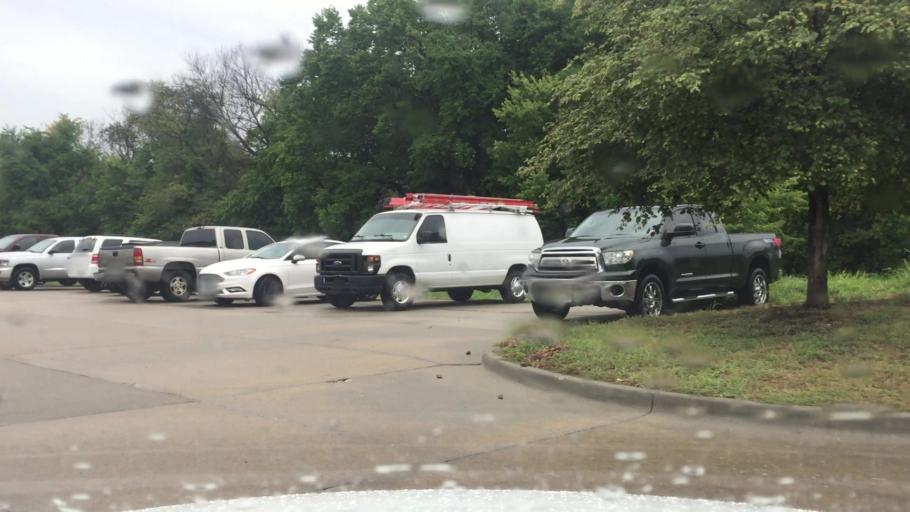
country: US
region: Missouri
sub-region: Jackson County
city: Lone Jack
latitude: 38.8805
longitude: -94.2102
